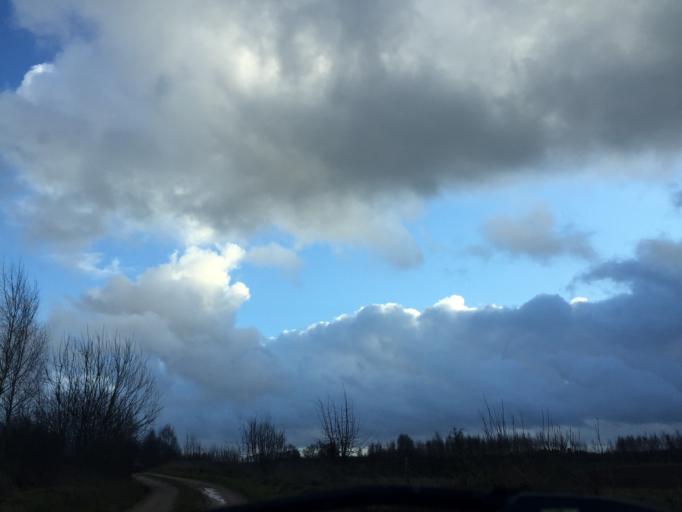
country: LV
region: Burtnieki
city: Matisi
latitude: 57.6820
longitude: 25.3050
